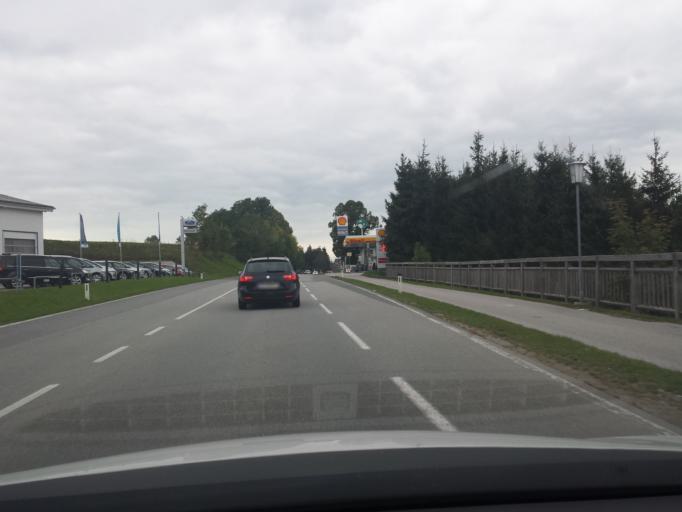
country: AT
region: Salzburg
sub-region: Politischer Bezirk Salzburg-Umgebung
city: Hof bei Salzburg
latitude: 47.8164
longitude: 13.2291
